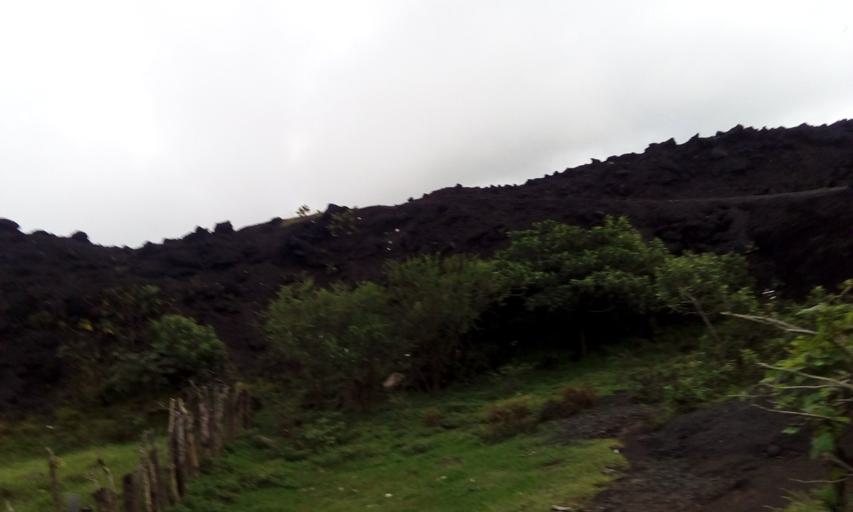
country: GT
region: Escuintla
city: San Vicente Pacaya
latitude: 14.3407
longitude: -90.6152
